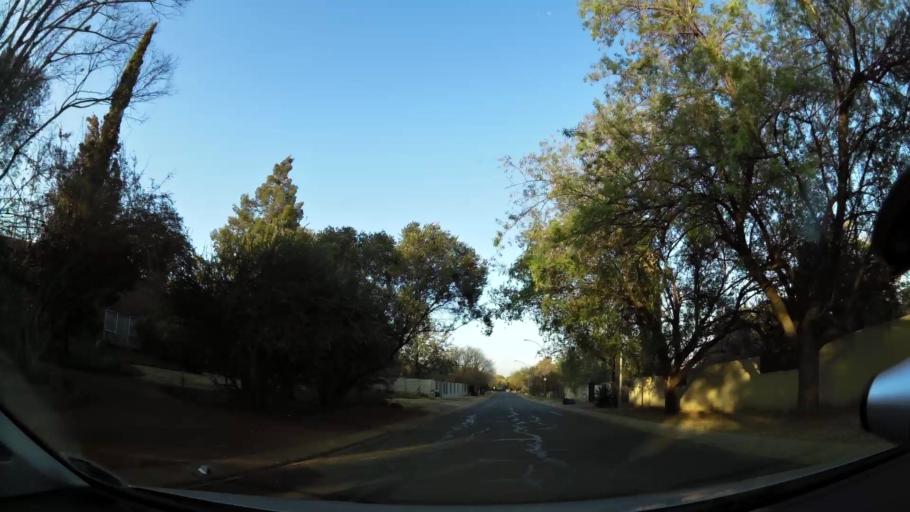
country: ZA
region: Orange Free State
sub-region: Mangaung Metropolitan Municipality
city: Bloemfontein
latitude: -29.0918
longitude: 26.1530
